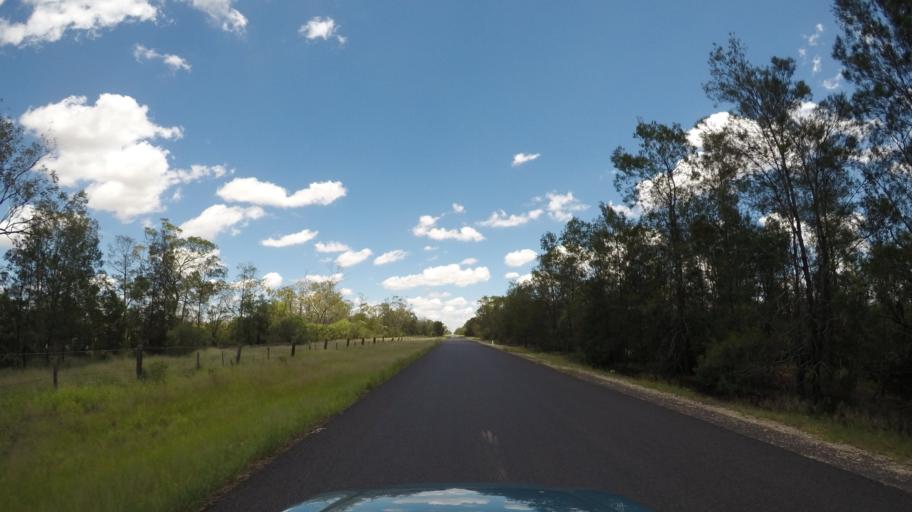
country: AU
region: Queensland
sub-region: Goondiwindi
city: Goondiwindi
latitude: -28.1670
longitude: 150.4476
